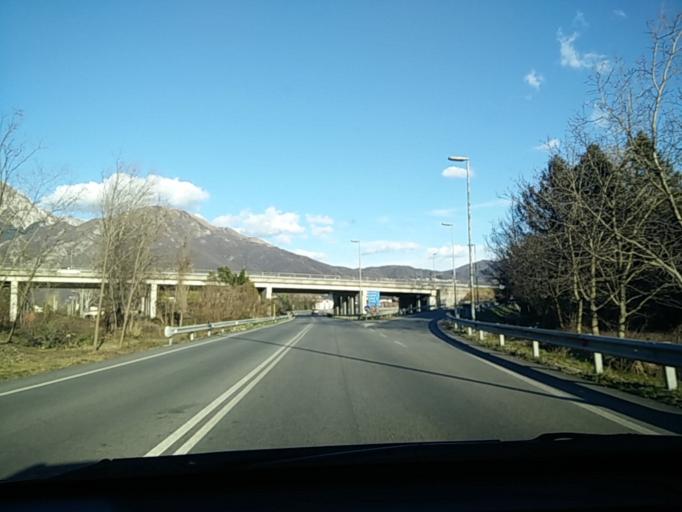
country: IT
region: Friuli Venezia Giulia
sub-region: Provincia di Udine
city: Gemona
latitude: 46.2587
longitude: 13.1077
